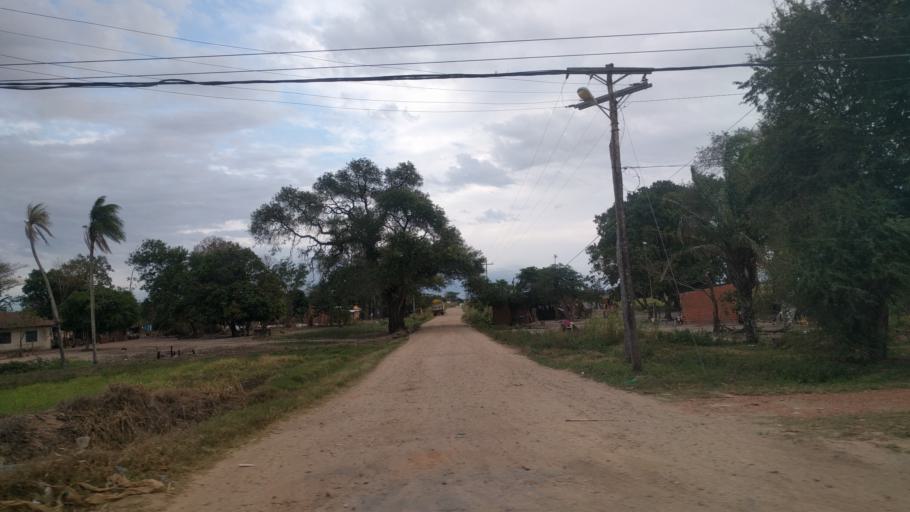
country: BO
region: Santa Cruz
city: Montero
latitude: -17.4001
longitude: -63.2096
